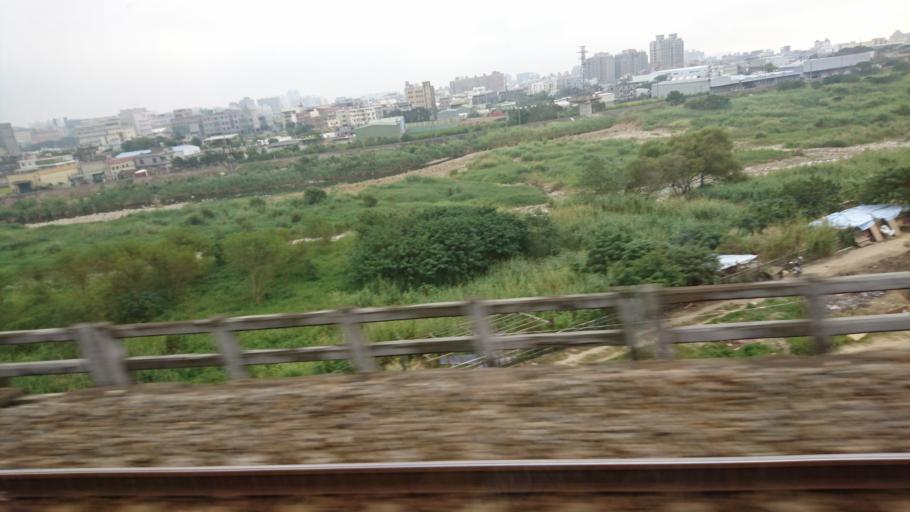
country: TW
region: Taiwan
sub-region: Hsinchu
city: Zhubei
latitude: 24.8541
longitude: 121.0106
